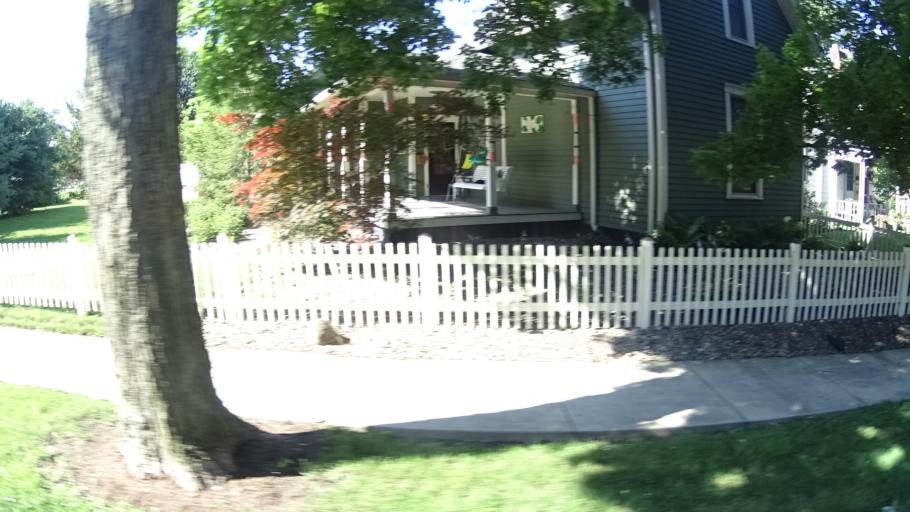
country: US
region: Indiana
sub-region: Madison County
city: Pendleton
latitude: 40.0017
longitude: -85.7409
